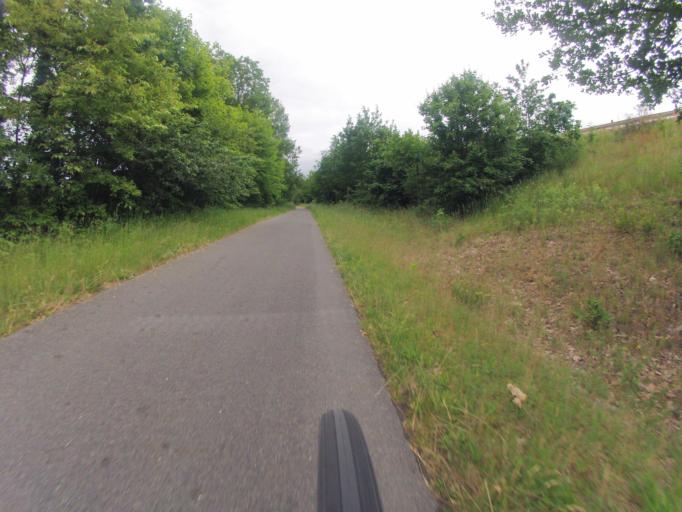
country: DE
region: North Rhine-Westphalia
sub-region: Regierungsbezirk Munster
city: Birgte
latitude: 52.2184
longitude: 7.6778
